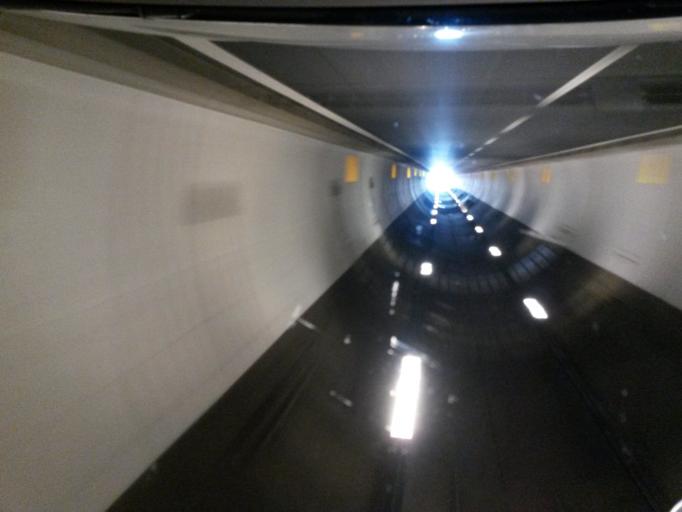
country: IT
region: Tuscany
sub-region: Provincia di Livorno
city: Collesalvetti
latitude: 43.5840
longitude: 10.4601
